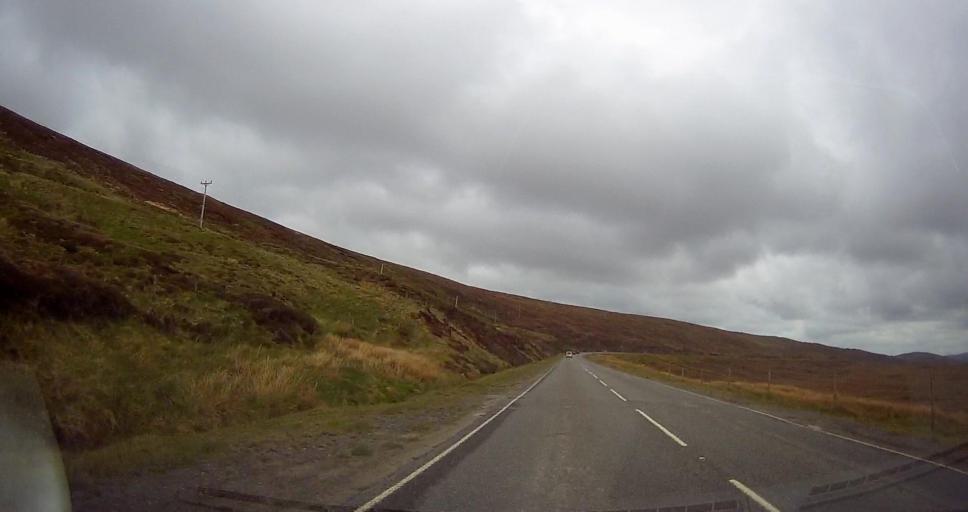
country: GB
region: Scotland
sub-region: Shetland Islands
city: Lerwick
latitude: 60.3081
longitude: -1.2439
